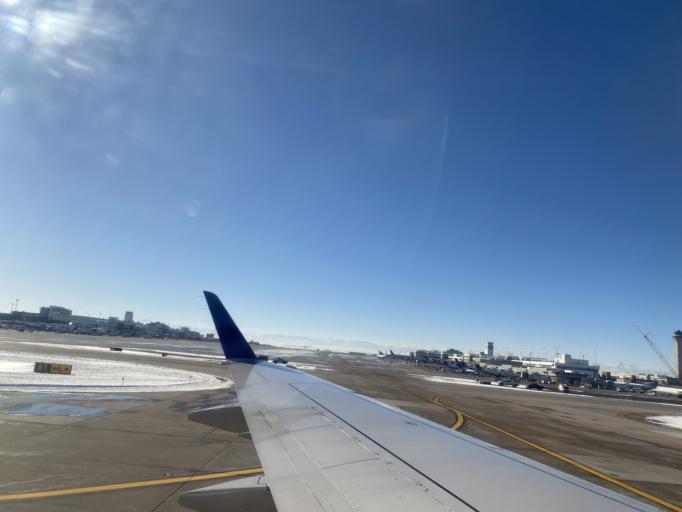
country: US
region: Colorado
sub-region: Weld County
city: Lochbuie
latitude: 39.8565
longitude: -104.6623
